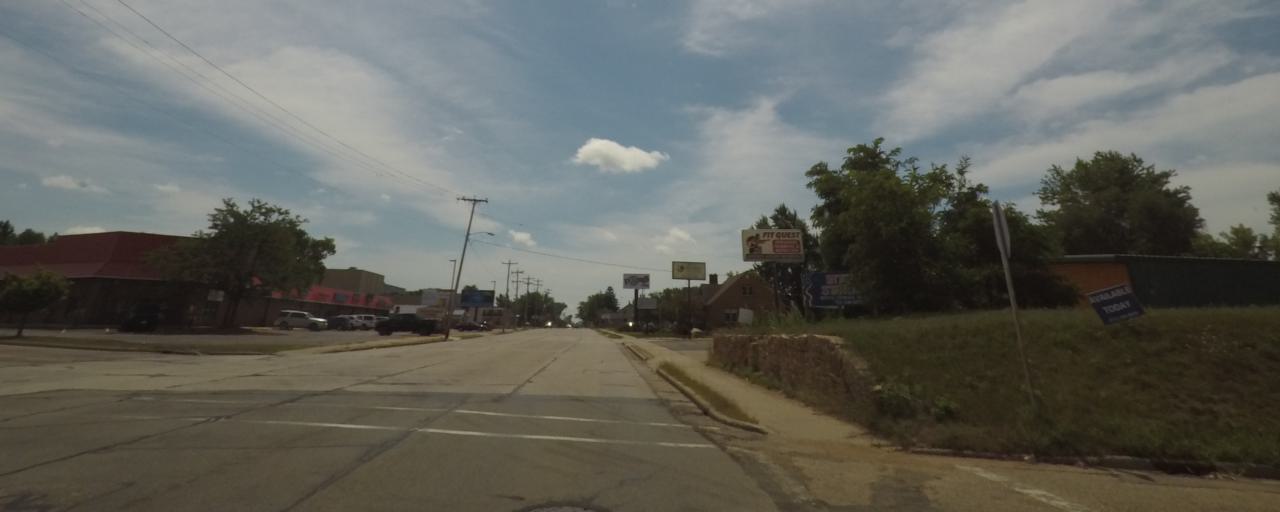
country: US
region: Wisconsin
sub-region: Portage County
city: Stevens Point
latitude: 44.5122
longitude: -89.5726
